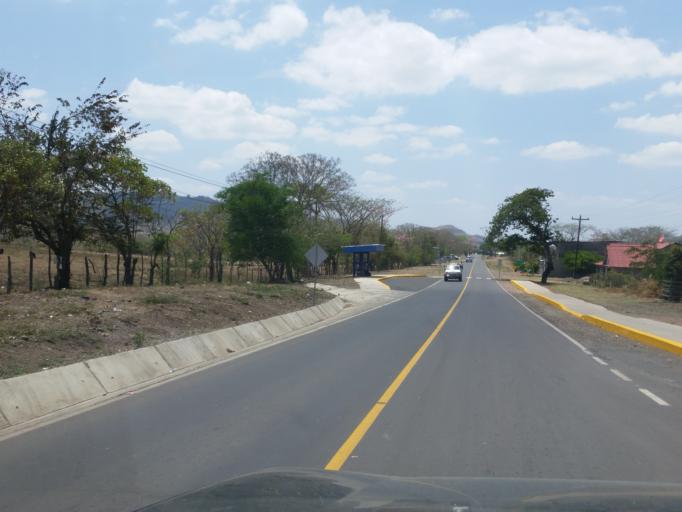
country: NI
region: Boaco
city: Boaco
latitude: 12.4895
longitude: -85.6393
